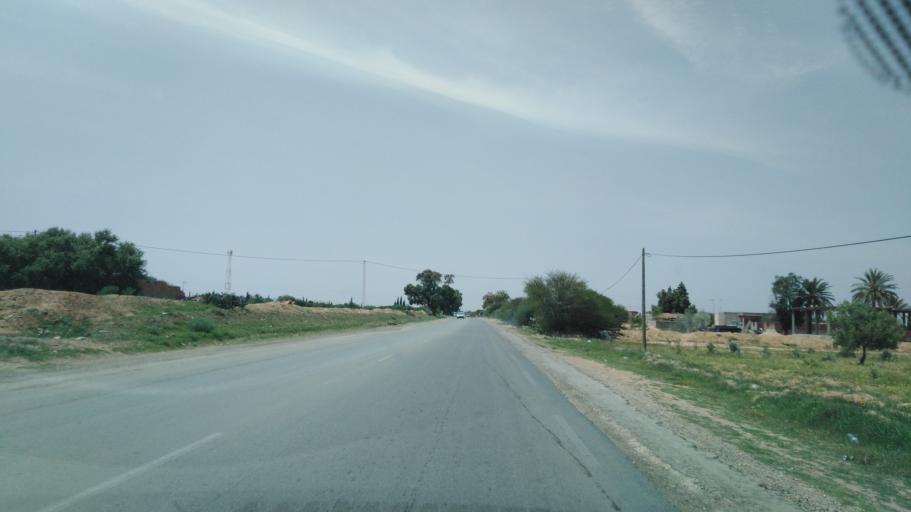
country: TN
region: Safaqis
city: Sfax
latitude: 34.7314
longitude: 10.5622
